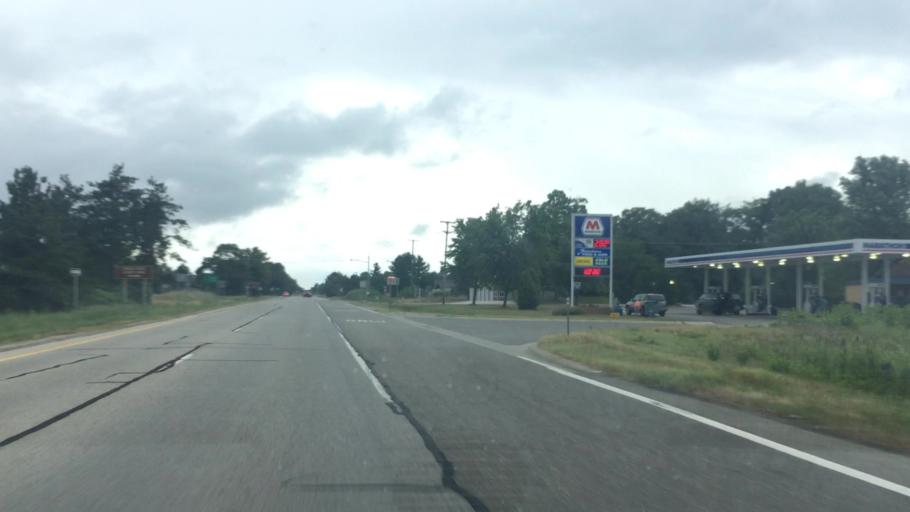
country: US
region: Michigan
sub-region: Ottawa County
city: Beechwood
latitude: 42.9345
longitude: -86.1557
